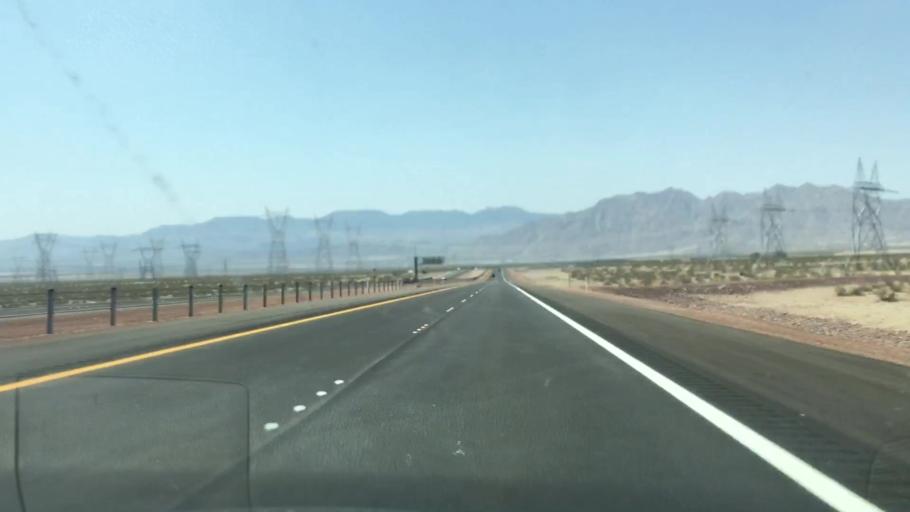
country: US
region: Nevada
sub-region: Clark County
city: Boulder City
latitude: 35.9343
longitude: -114.8433
